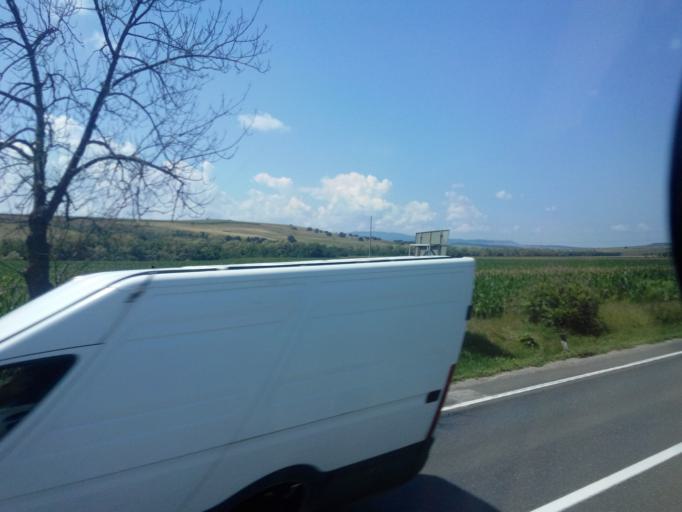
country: RO
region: Sibiu
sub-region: Oras Miercurea Sibiului
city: Miercurea Sibiului
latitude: 45.8911
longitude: 23.7736
